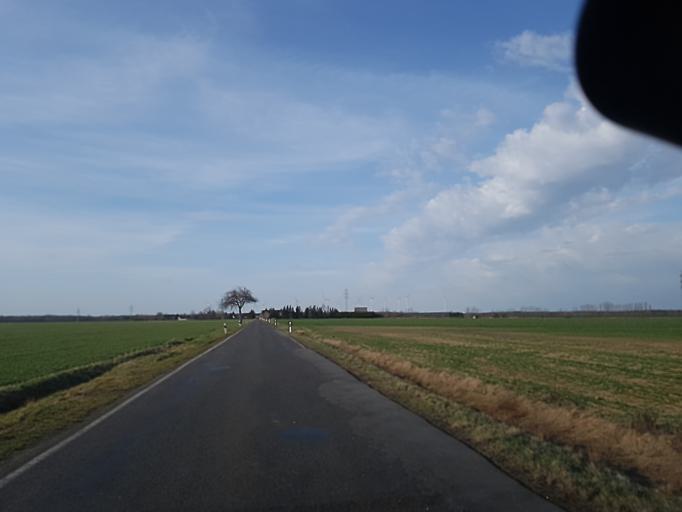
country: DE
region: Brandenburg
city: Falkenberg
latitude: 51.5379
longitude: 13.2950
